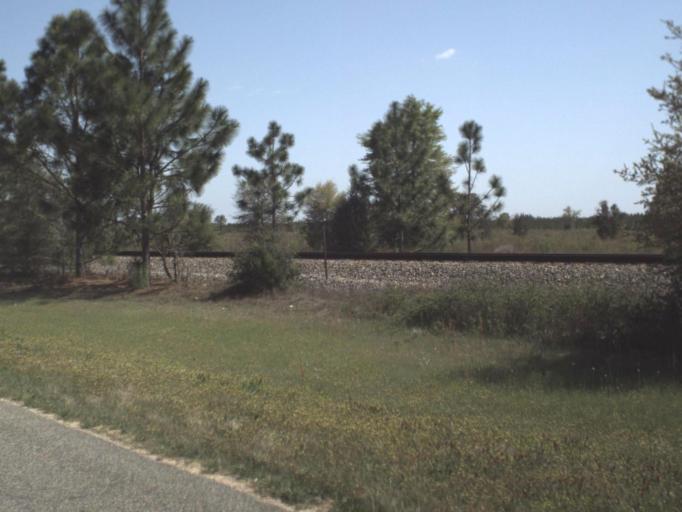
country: US
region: Florida
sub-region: Okaloosa County
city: Crestview
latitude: 30.7497
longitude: -86.4261
